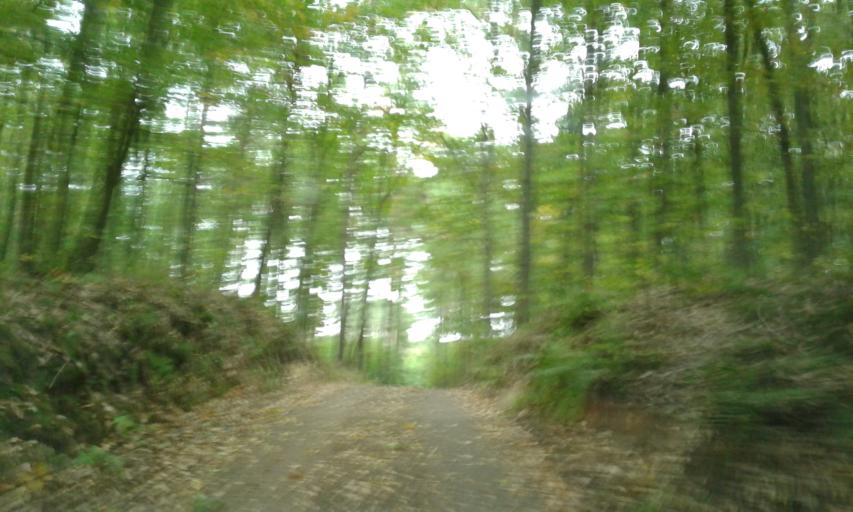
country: PL
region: West Pomeranian Voivodeship
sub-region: Powiat choszczenski
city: Pelczyce
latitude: 53.0900
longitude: 15.2452
